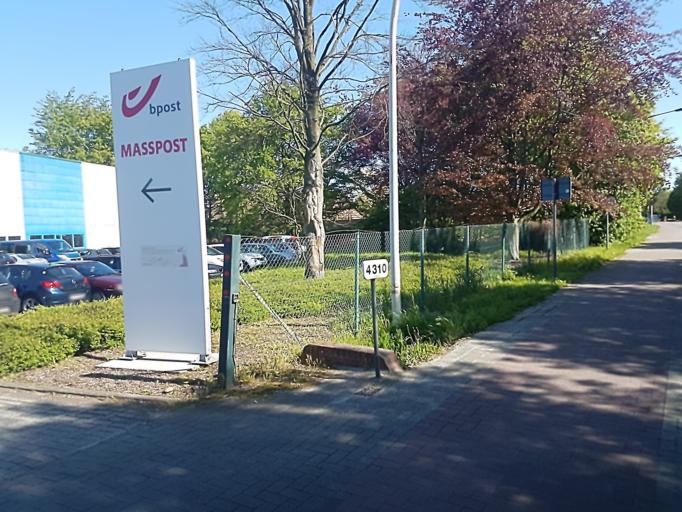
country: BE
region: Flanders
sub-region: Provincie Antwerpen
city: Turnhout
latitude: 51.3027
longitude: 4.9338
